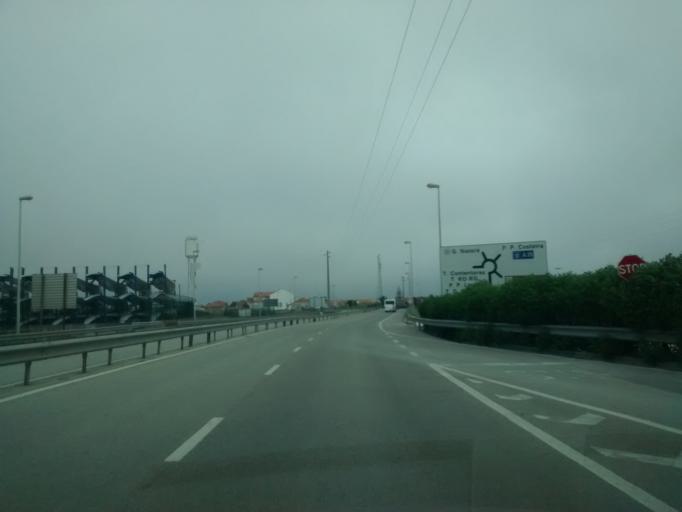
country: PT
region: Aveiro
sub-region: Ilhavo
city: Gafanha da Nazare
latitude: 40.6418
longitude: -8.7277
